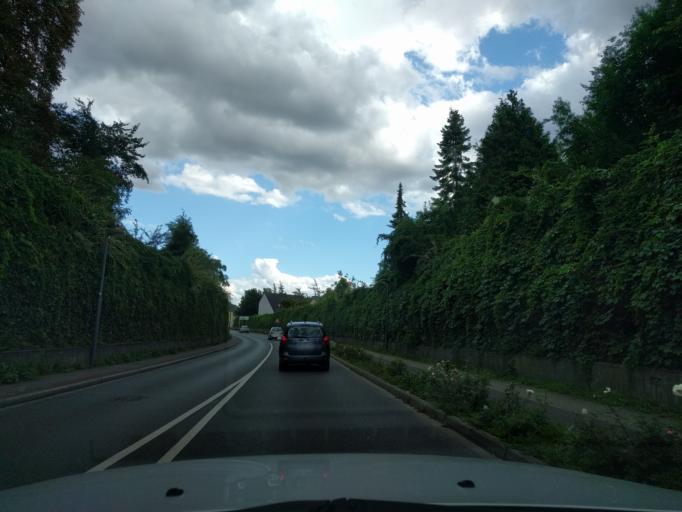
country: DE
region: North Rhine-Westphalia
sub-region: Regierungsbezirk Dusseldorf
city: Ratingen
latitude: 51.3018
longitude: 6.8558
